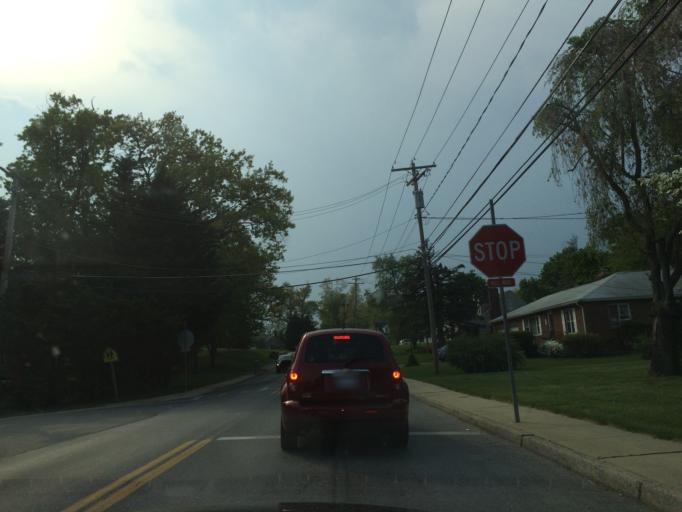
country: US
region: Maryland
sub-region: Carroll County
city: Mount Airy
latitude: 39.3695
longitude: -77.1507
